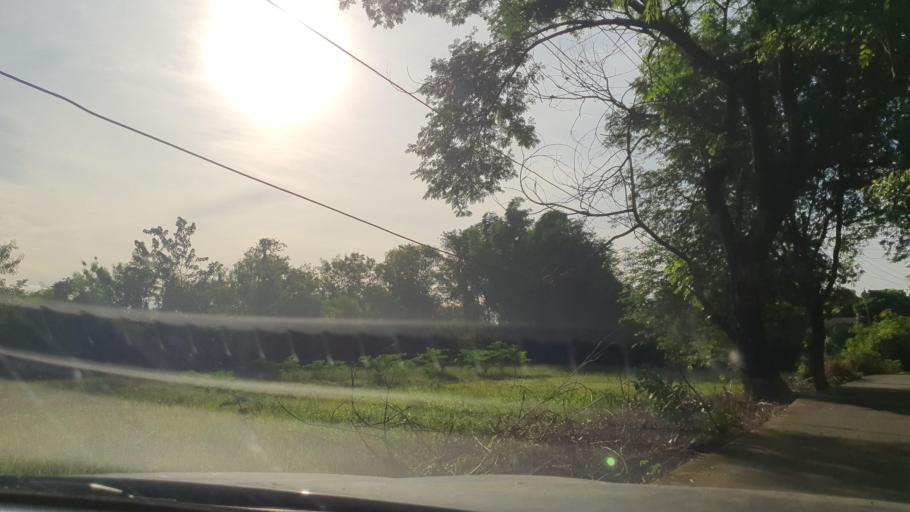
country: TH
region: Chiang Mai
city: San Kamphaeng
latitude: 18.7438
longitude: 99.1098
